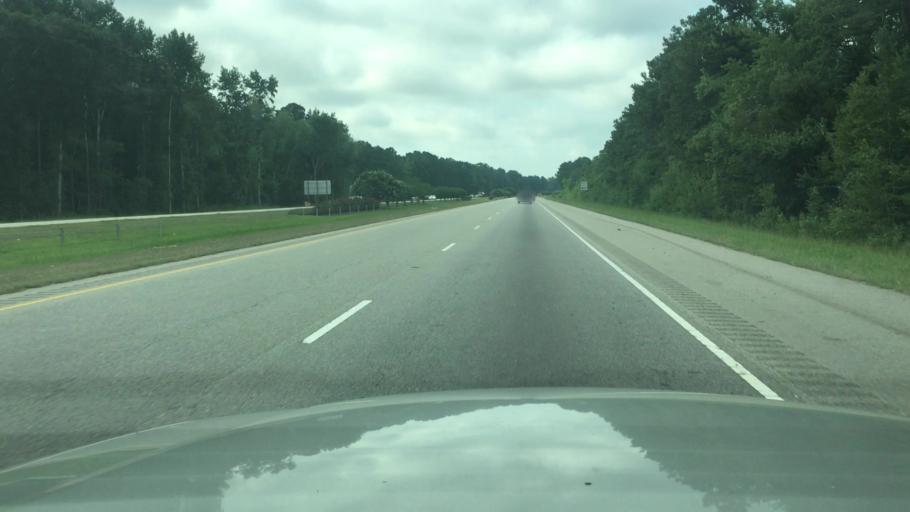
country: US
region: North Carolina
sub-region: Cumberland County
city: Fayetteville
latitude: 35.0017
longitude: -78.8655
